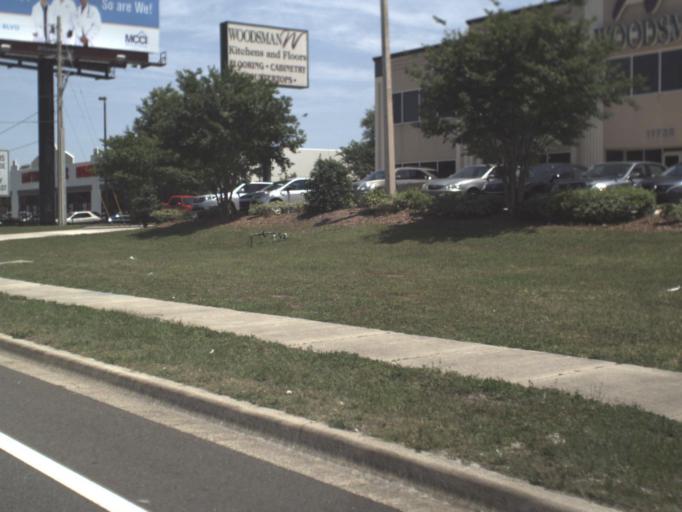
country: US
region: Florida
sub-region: Duval County
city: Neptune Beach
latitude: 30.2869
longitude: -81.5147
